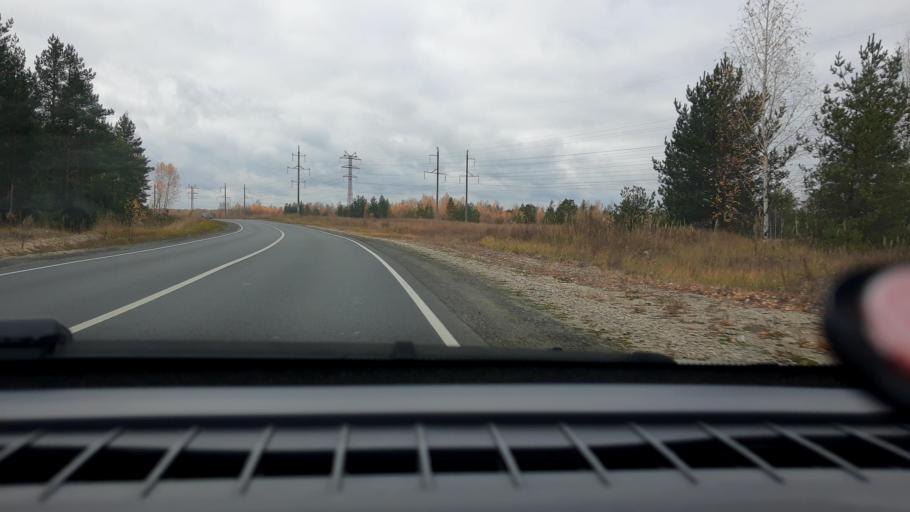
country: RU
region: Nizjnij Novgorod
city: Lukino
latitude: 56.3600
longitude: 43.5961
